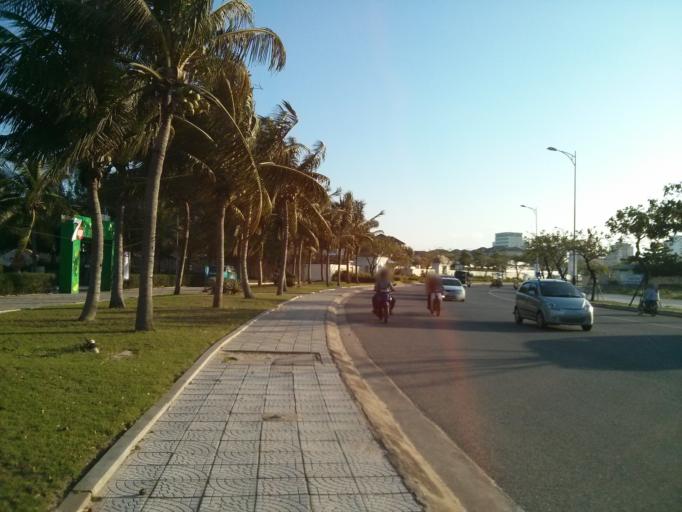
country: VN
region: Da Nang
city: Son Tra
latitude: 16.0469
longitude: 108.2496
